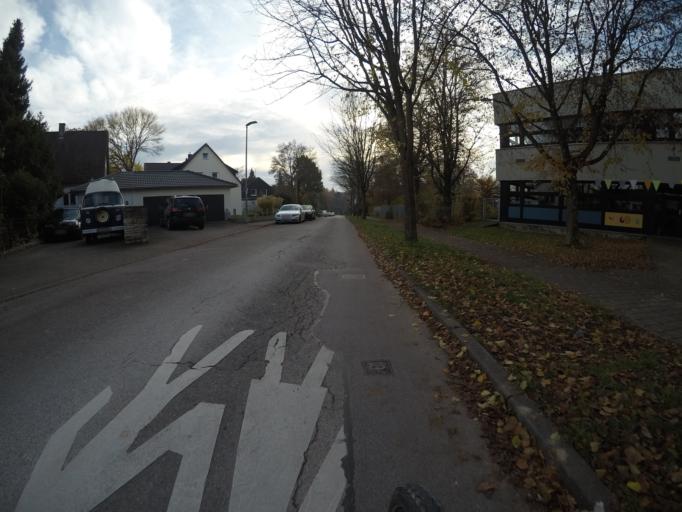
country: DE
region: Baden-Wuerttemberg
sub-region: Regierungsbezirk Stuttgart
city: Leinfelden-Echterdingen
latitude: 48.6900
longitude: 9.1388
